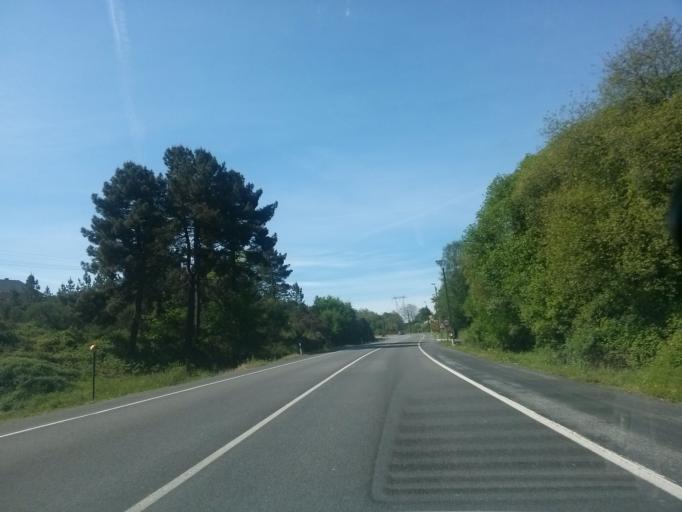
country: ES
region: Galicia
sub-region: Provincia de Lugo
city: Lugo
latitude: 42.9918
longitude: -7.5883
